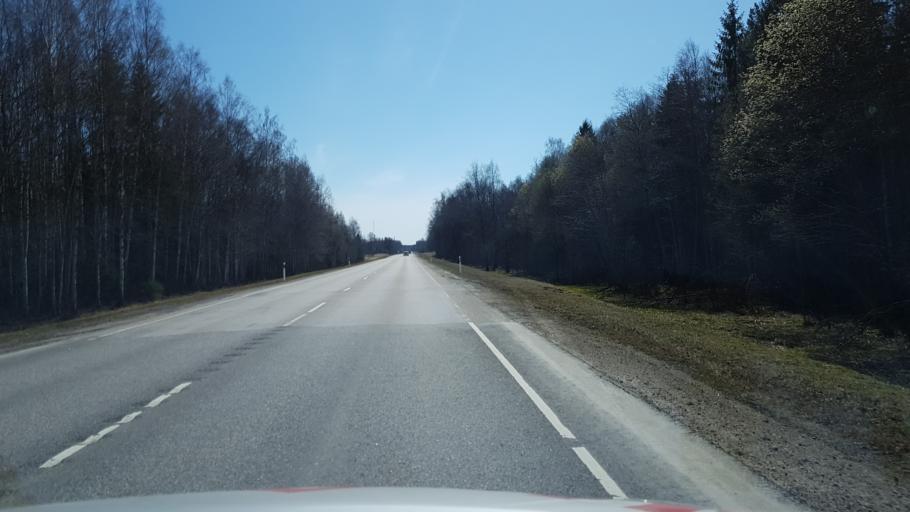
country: EE
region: Ida-Virumaa
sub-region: Johvi vald
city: Johvi
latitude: 59.1827
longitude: 27.3480
